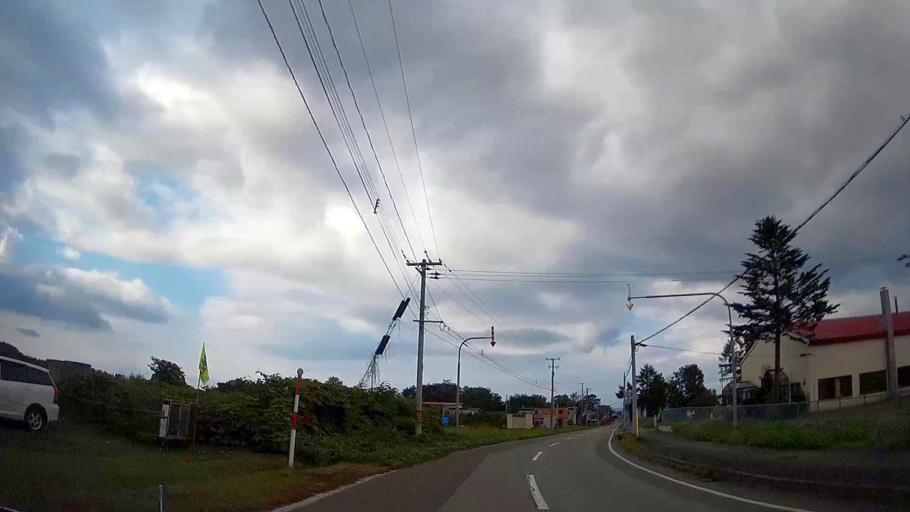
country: JP
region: Hokkaido
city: Nanae
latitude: 42.0994
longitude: 140.5610
